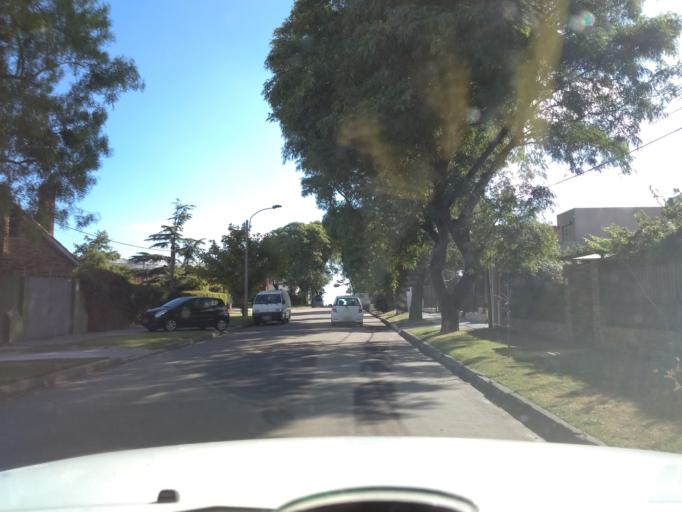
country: UY
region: Canelones
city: Paso de Carrasco
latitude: -34.8933
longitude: -56.0827
